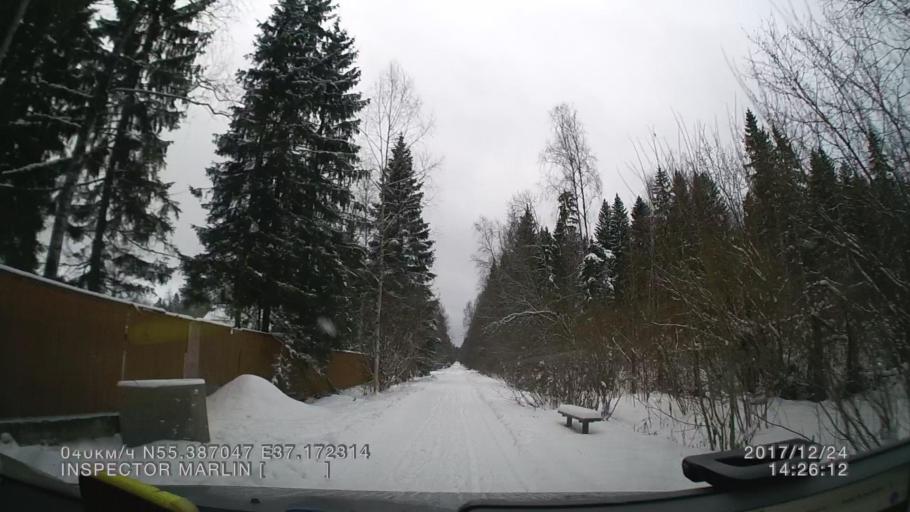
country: RU
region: Moskovskaya
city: Troitsk
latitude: 55.3869
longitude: 37.1721
